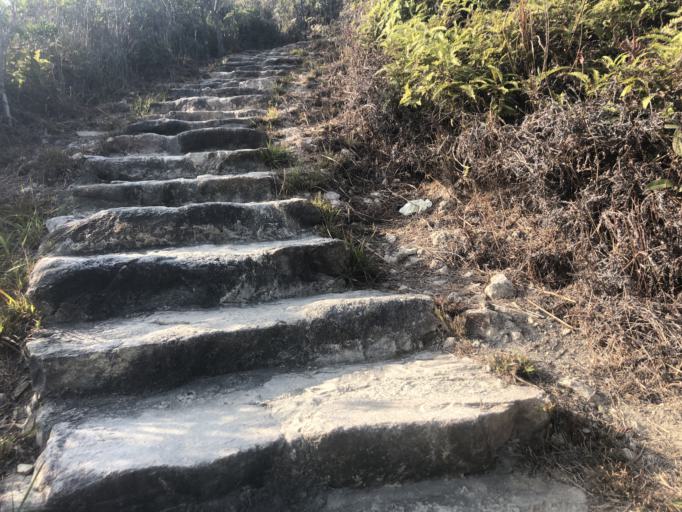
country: HK
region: Sai Kung
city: Sai Kung
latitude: 22.3596
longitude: 114.2950
